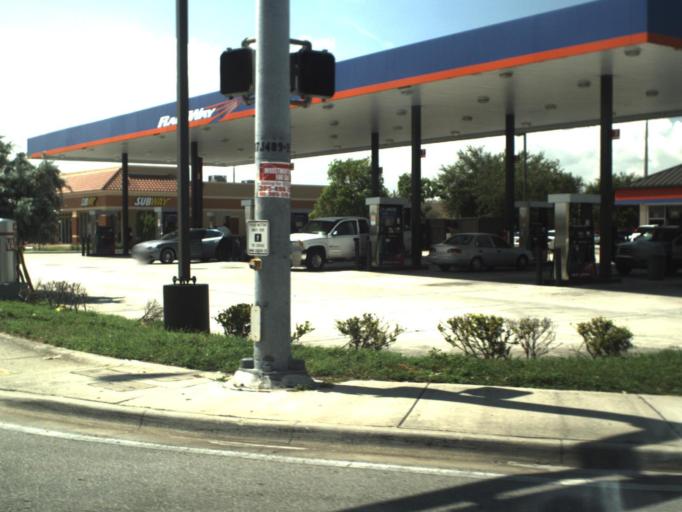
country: US
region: Florida
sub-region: Miami-Dade County
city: Norland
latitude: 25.9423
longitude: -80.2133
